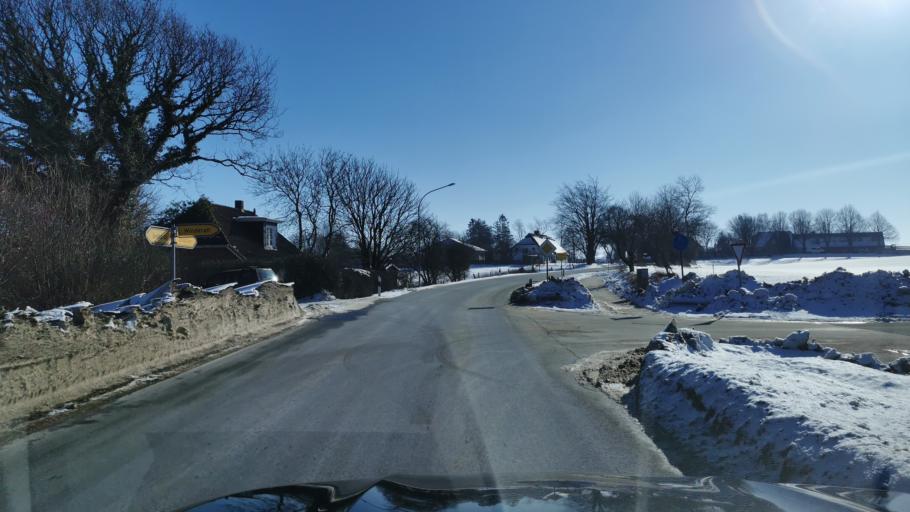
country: DE
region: Schleswig-Holstein
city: Sorup
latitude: 54.7344
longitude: 9.6483
